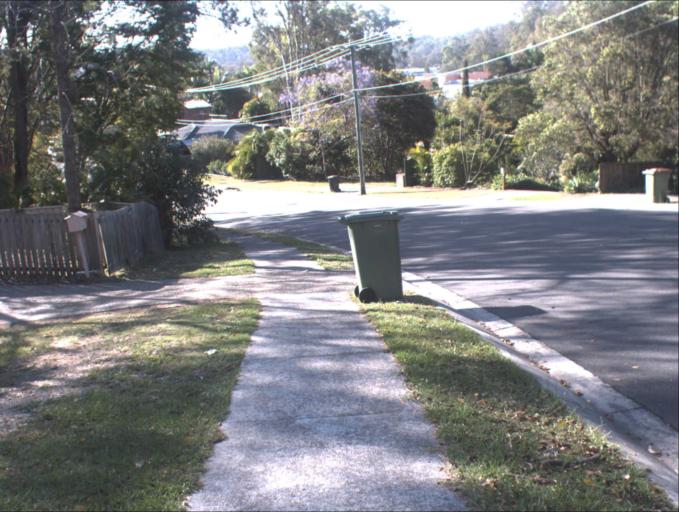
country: AU
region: Queensland
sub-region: Logan
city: Beenleigh
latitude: -27.7201
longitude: 153.1858
